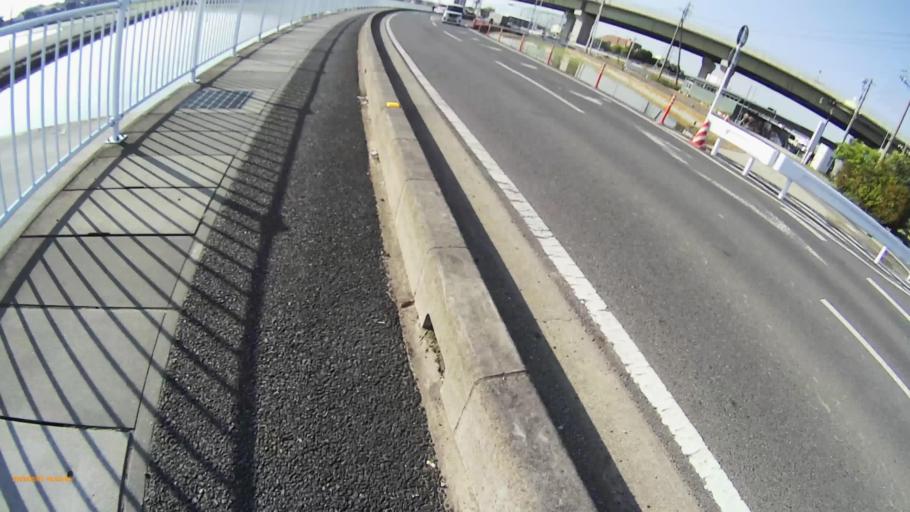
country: JP
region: Saitama
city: Satte
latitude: 36.0628
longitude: 139.7120
